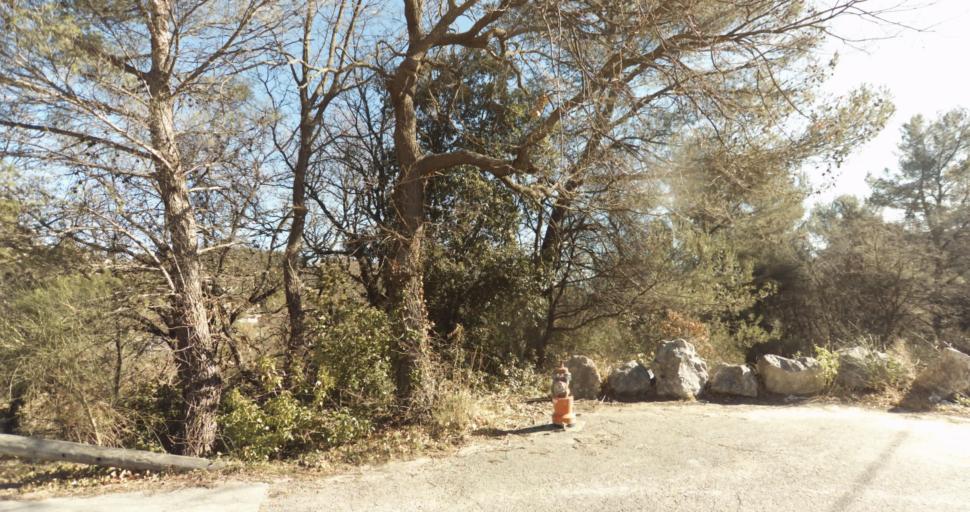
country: FR
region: Provence-Alpes-Cote d'Azur
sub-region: Departement des Bouches-du-Rhone
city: Peypin
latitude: 43.3815
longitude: 5.5766
